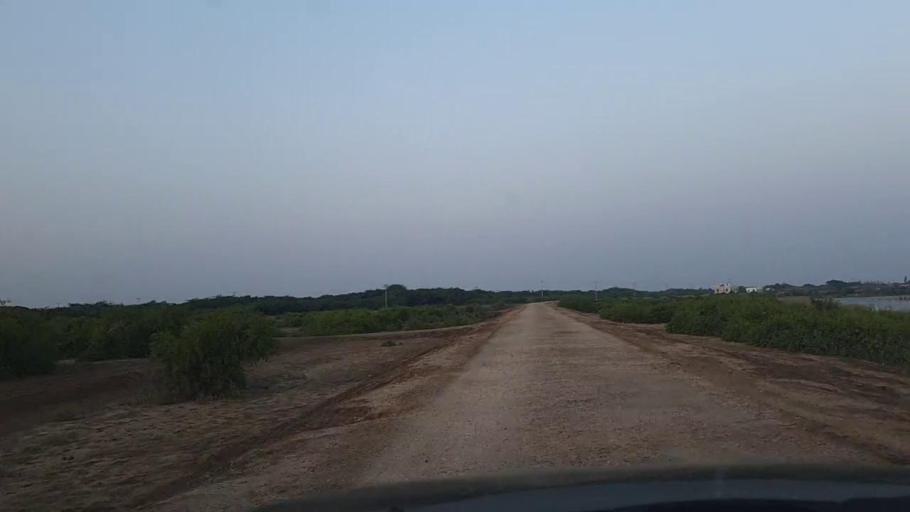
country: PK
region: Sindh
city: Mirpur Sakro
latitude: 24.6373
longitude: 67.6615
